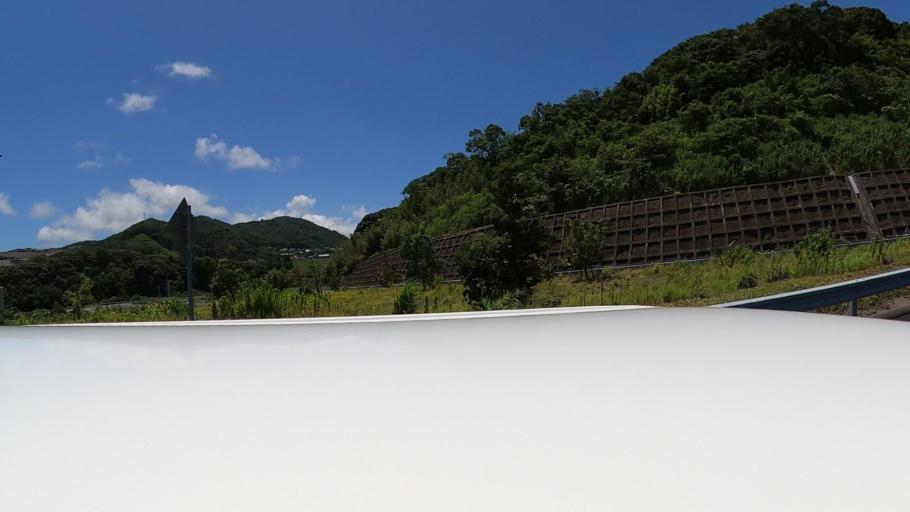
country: JP
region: Miyazaki
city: Nobeoka
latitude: 32.4015
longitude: 131.6161
